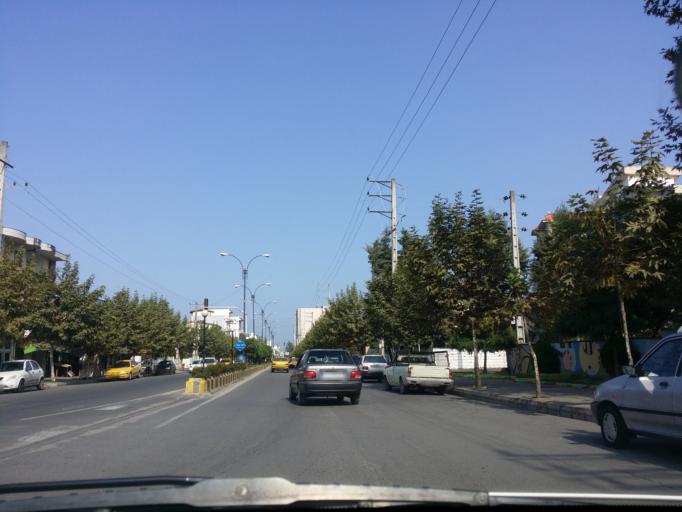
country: IR
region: Mazandaran
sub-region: Nowshahr
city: Nowshahr
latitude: 36.6415
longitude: 51.4907
